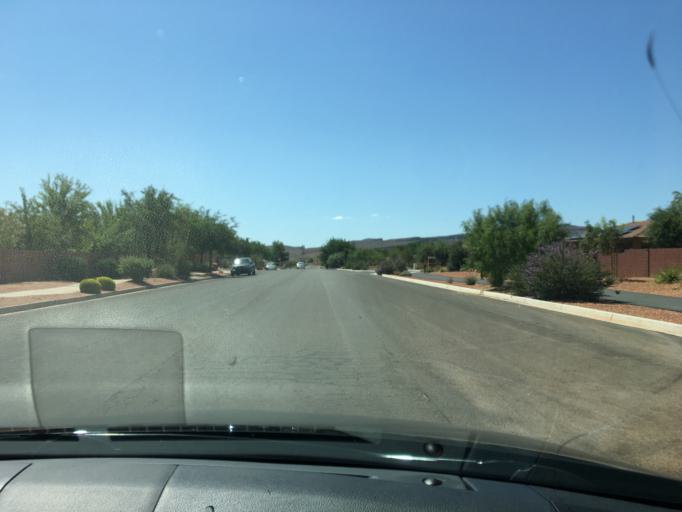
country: US
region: Utah
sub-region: Washington County
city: Ivins
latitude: 37.1627
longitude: -113.6887
